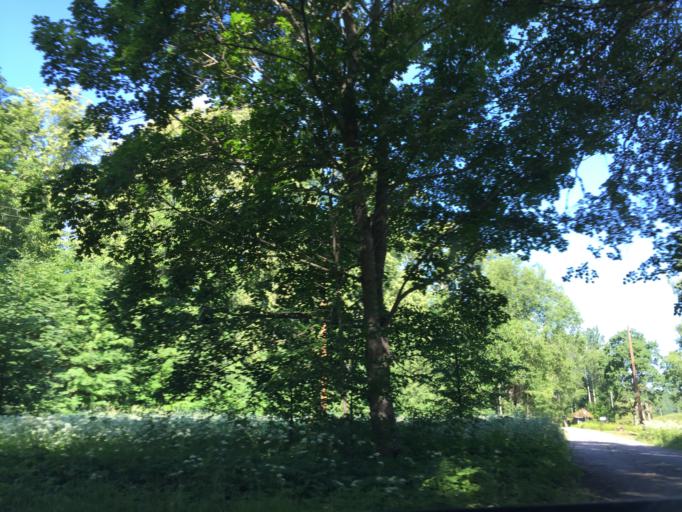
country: LV
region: Kuldigas Rajons
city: Kuldiga
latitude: 57.3219
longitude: 22.0425
